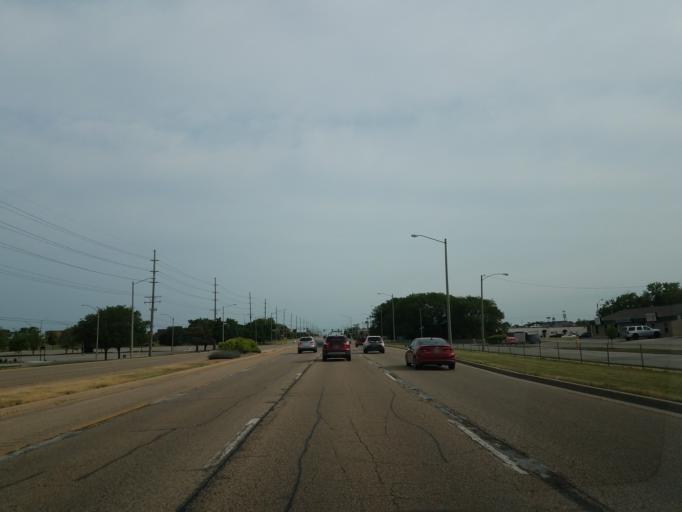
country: US
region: Illinois
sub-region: McLean County
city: Bloomington
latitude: 40.4776
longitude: -88.9525
